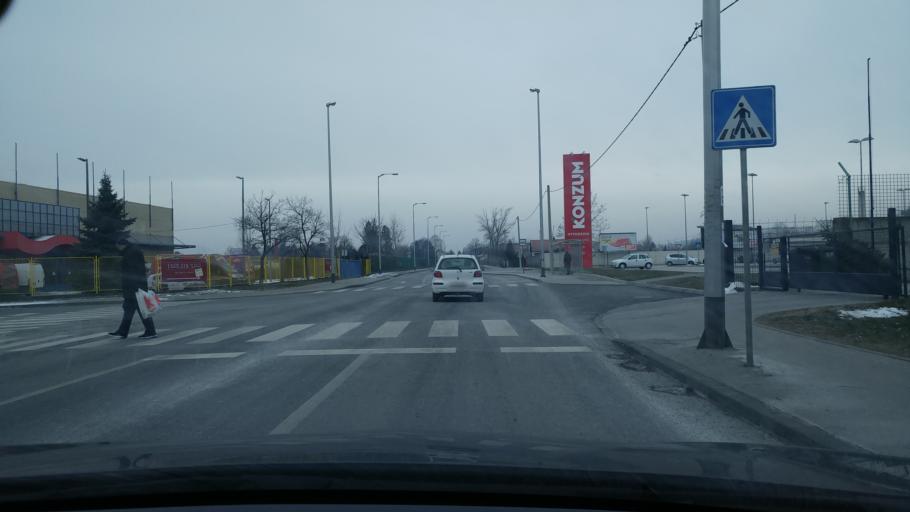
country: HR
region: Grad Zagreb
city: Stenjevec
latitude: 45.8118
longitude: 15.8844
